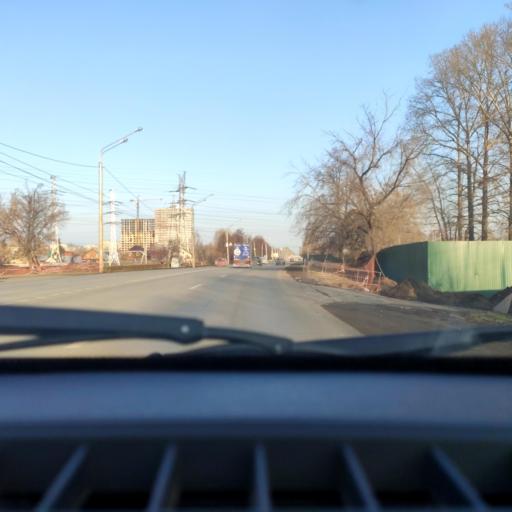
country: RU
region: Bashkortostan
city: Avdon
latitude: 54.6925
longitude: 55.8190
